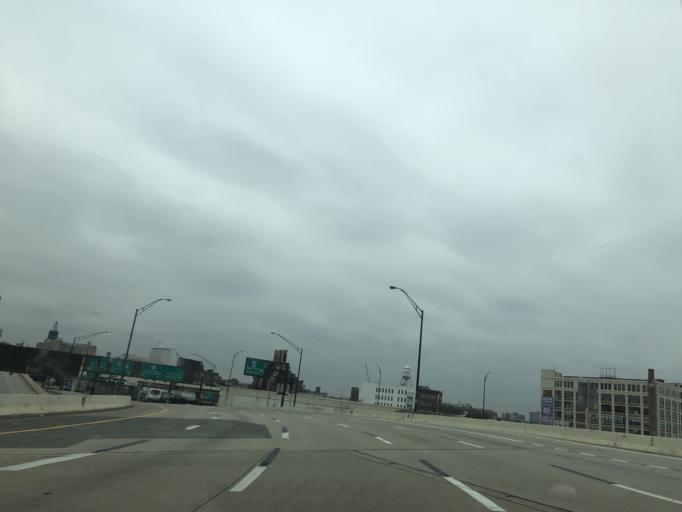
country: US
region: Pennsylvania
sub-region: Philadelphia County
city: Philadelphia
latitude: 39.9562
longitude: -75.1485
